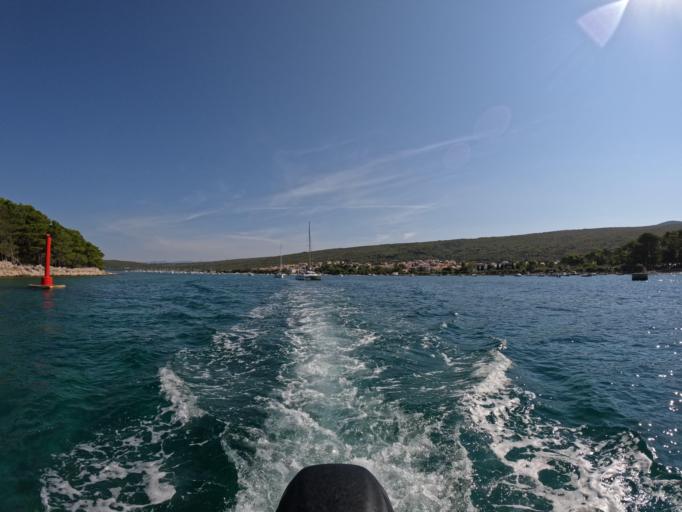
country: HR
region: Primorsko-Goranska
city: Punat
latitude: 45.0153
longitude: 14.6233
